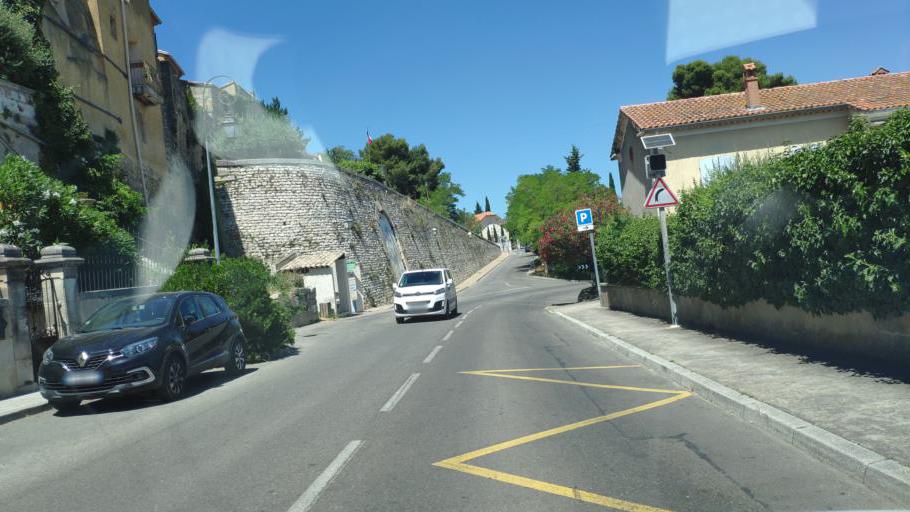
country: FR
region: Provence-Alpes-Cote d'Azur
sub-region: Departement du Vaucluse
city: Chateauneuf-de-Gadagne
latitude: 43.9281
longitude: 4.9457
